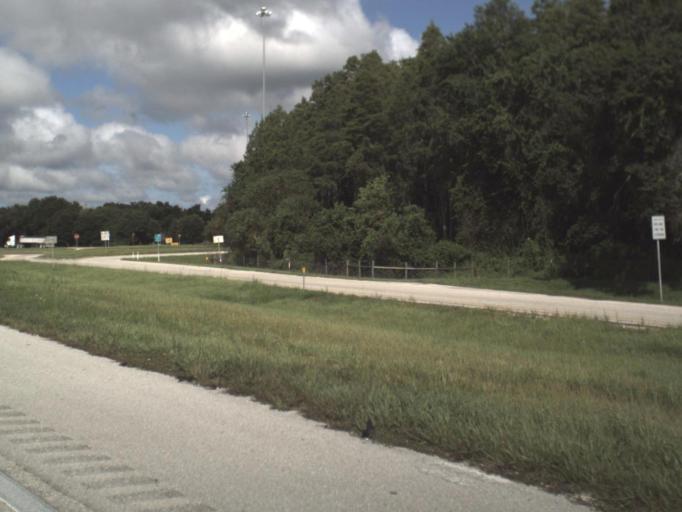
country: US
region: Florida
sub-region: Polk County
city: Gibsonia
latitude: 28.1411
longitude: -81.8959
